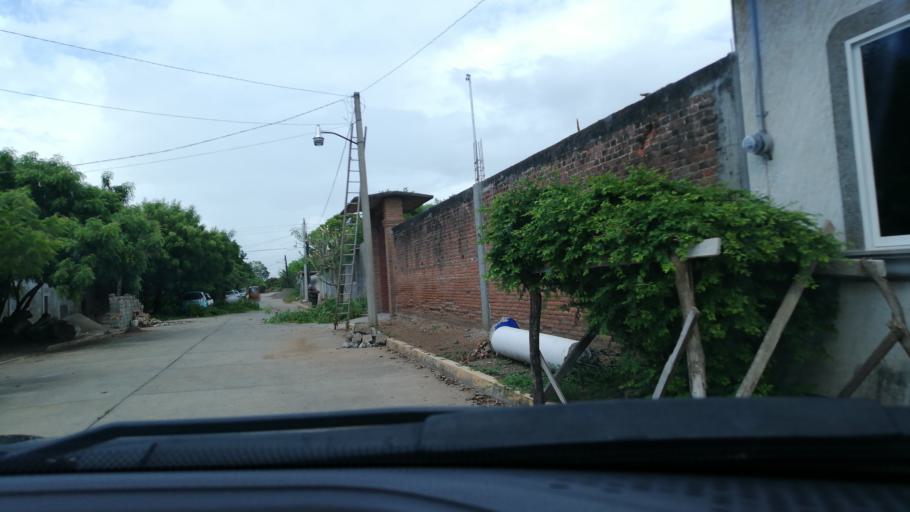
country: MX
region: Oaxaca
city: Asuncion Ixtaltepec
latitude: 16.5067
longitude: -95.0497
